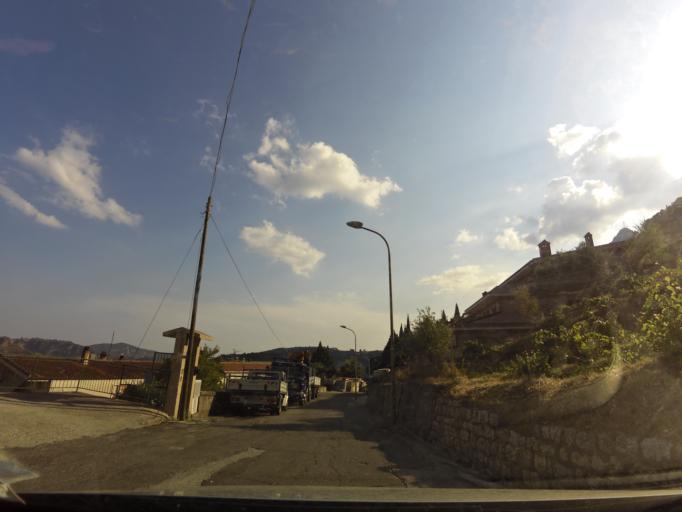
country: IT
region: Calabria
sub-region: Provincia di Reggio Calabria
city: Stilo
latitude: 38.4754
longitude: 16.4634
